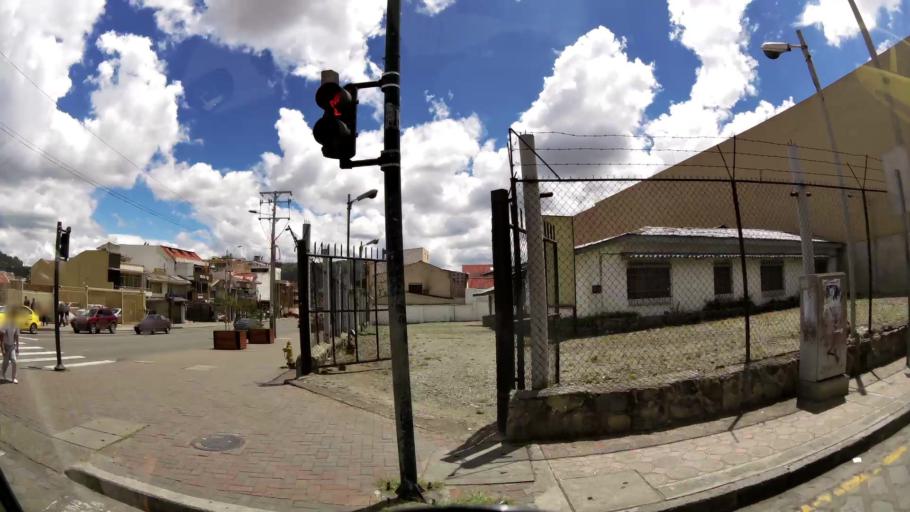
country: EC
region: Azuay
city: Cuenca
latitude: -2.8998
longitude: -78.9969
